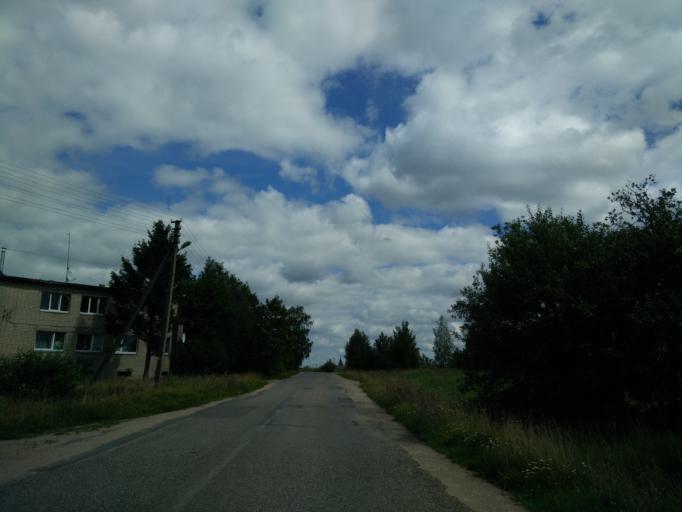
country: LT
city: Trakai
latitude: 54.6113
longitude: 24.9812
